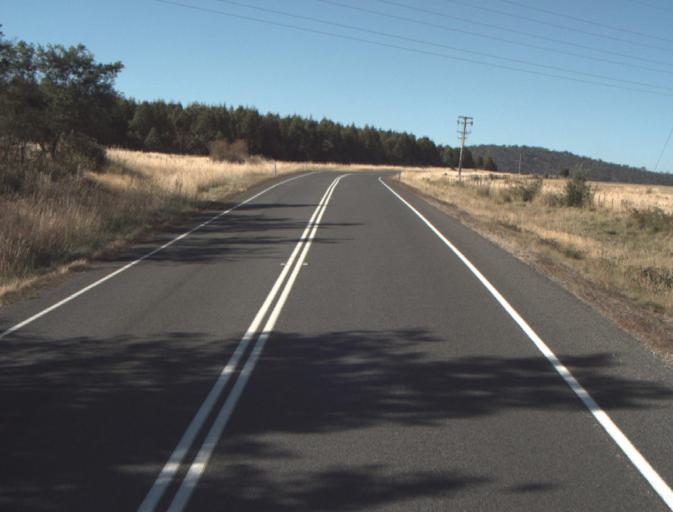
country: AU
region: Tasmania
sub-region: Launceston
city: Newstead
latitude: -41.4088
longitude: 147.2807
